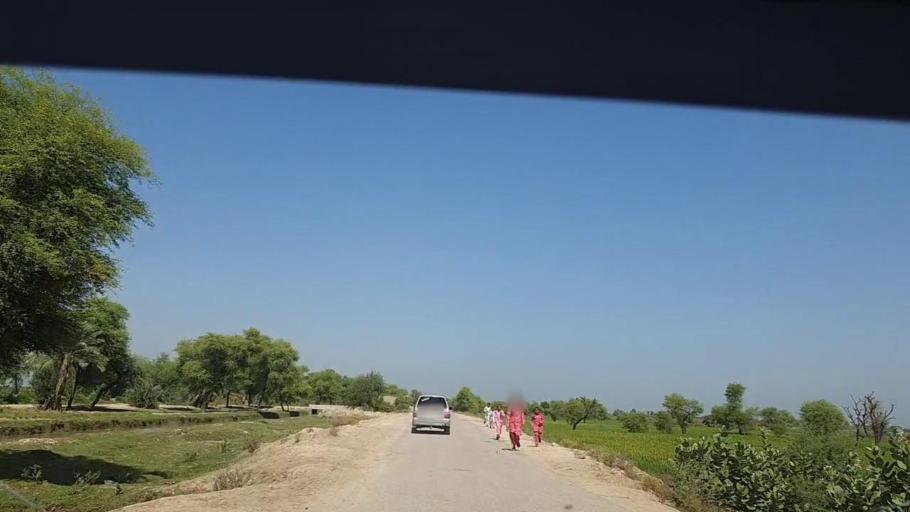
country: PK
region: Sindh
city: Kandhkot
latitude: 28.3031
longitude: 69.1110
